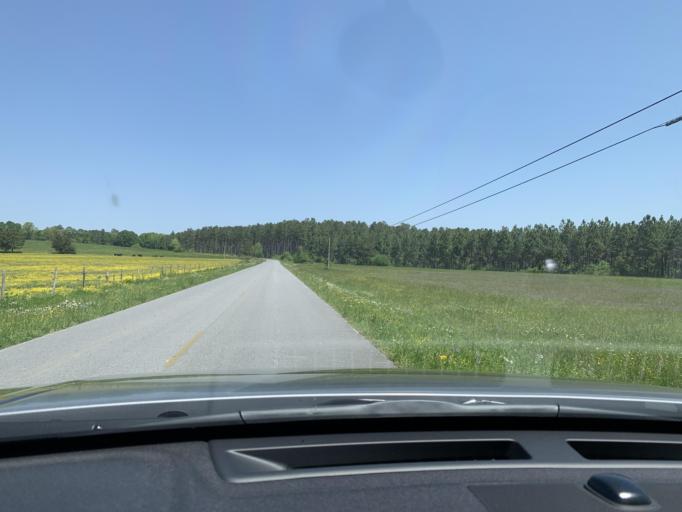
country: US
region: Georgia
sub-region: Polk County
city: Cedartown
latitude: 34.0484
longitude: -85.1856
